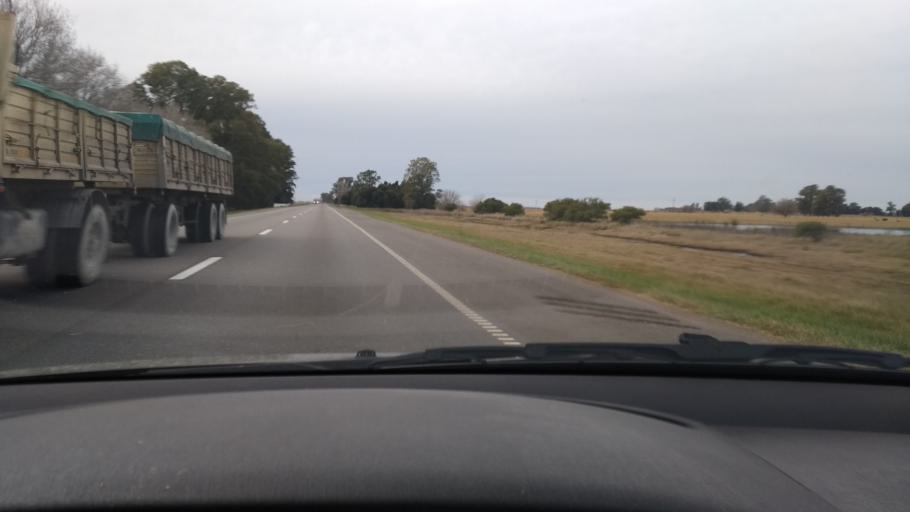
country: AR
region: Buenos Aires
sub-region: Partido de Las Flores
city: Las Flores
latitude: -36.3820
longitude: -59.4852
